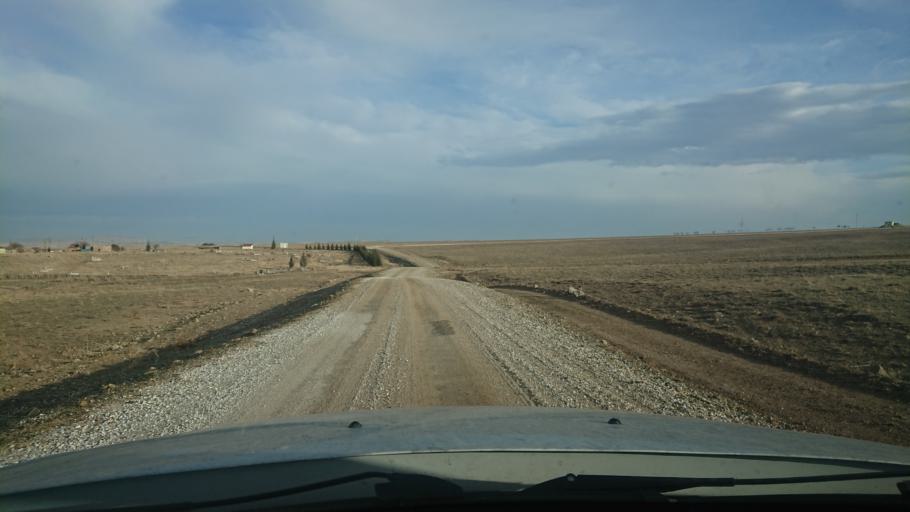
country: TR
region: Aksaray
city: Agacoren
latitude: 38.7133
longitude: 33.8688
